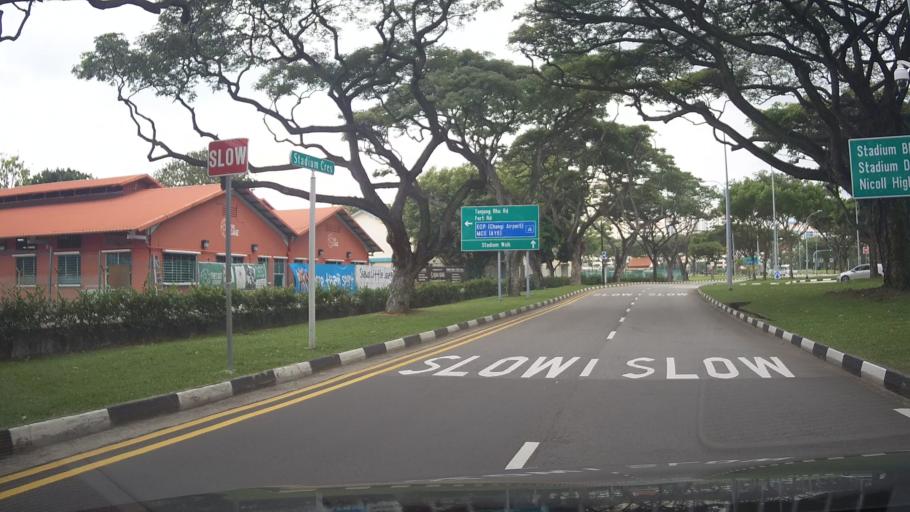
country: SG
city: Singapore
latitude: 1.3022
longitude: 103.8796
